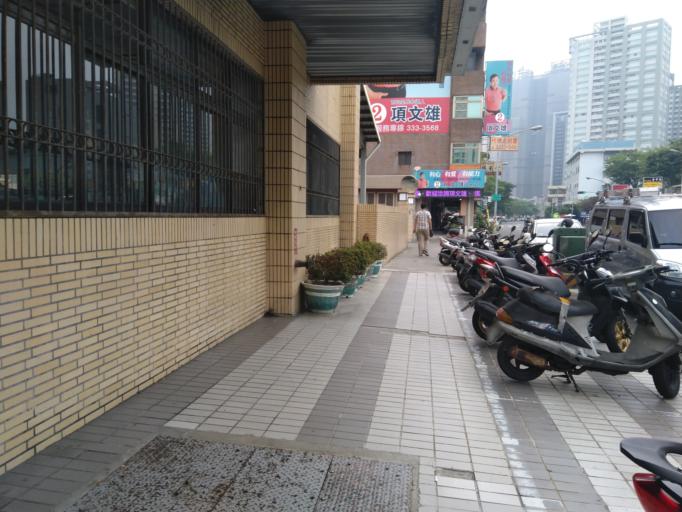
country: TW
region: Kaohsiung
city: Kaohsiung
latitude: 22.6097
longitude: 120.3099
